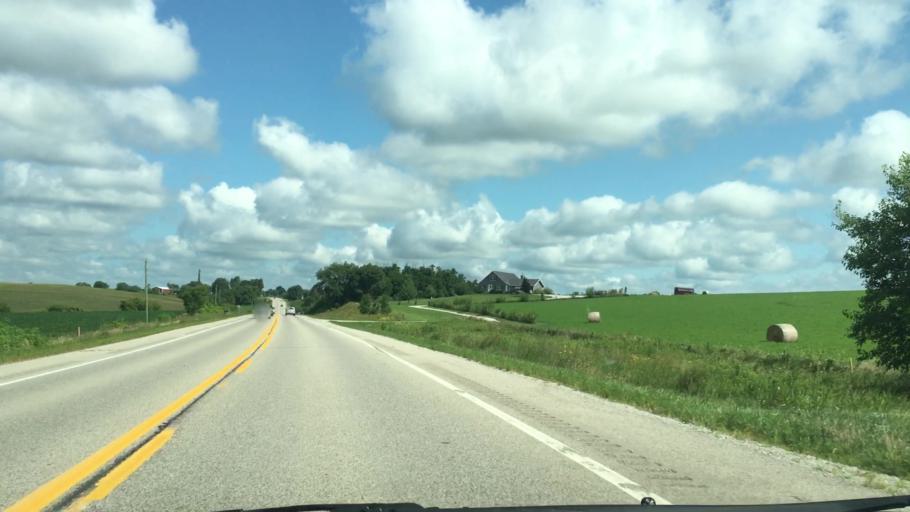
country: US
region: Iowa
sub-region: Johnson County
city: Solon
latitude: 41.7515
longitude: -91.4739
